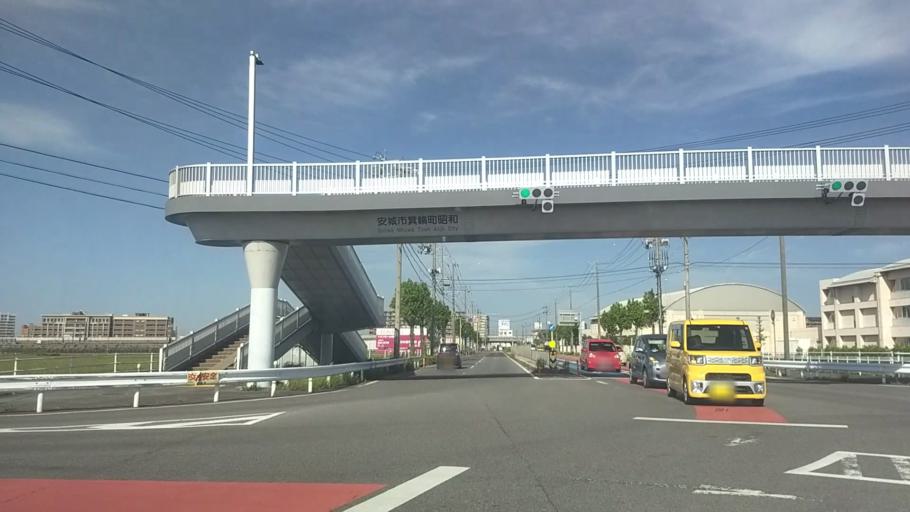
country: JP
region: Aichi
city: Anjo
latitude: 34.9603
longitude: 137.0625
